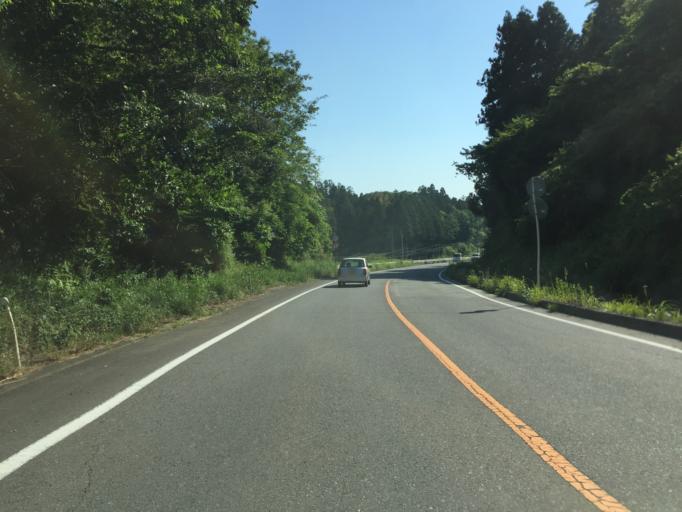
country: JP
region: Fukushima
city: Iwaki
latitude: 36.9450
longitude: 140.8241
